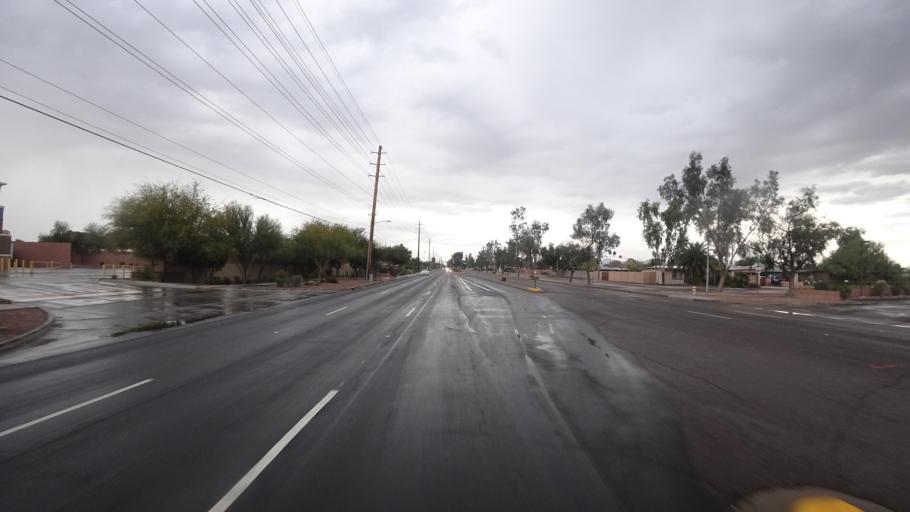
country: US
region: Arizona
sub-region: Maricopa County
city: Scottsdale
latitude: 33.4673
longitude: -111.9089
